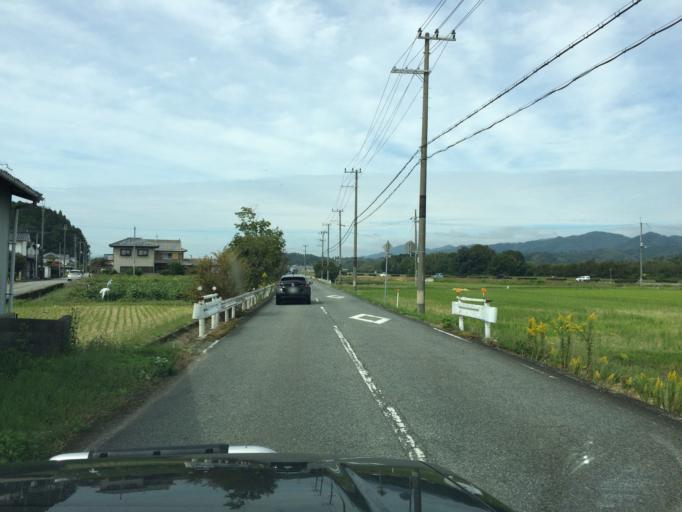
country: JP
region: Hyogo
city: Sasayama
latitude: 35.0693
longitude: 135.2694
